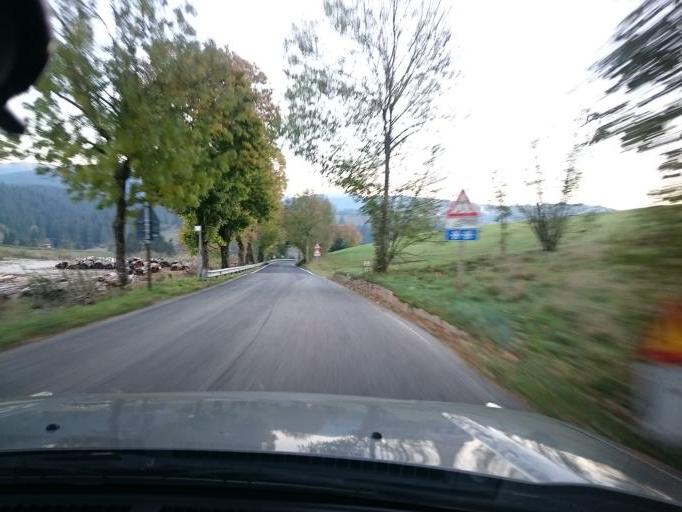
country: IT
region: Veneto
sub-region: Provincia di Vicenza
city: Canove di Roana
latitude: 45.8580
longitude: 11.4571
